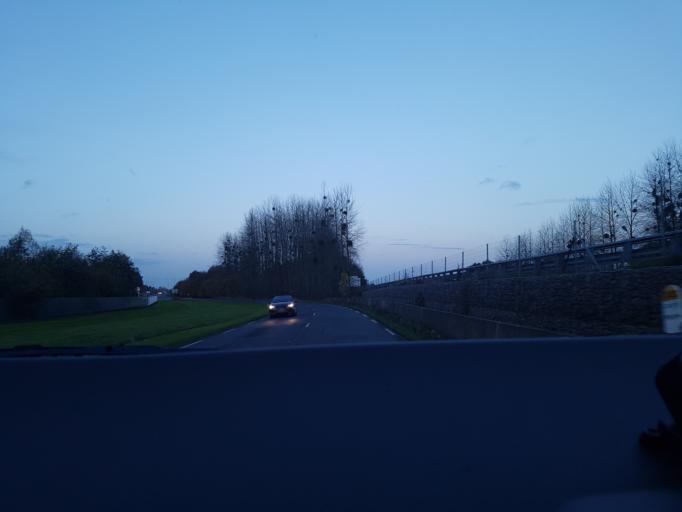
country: FR
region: Haute-Normandie
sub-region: Departement de l'Eure
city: Beuzeville
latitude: 49.3334
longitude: 0.3504
